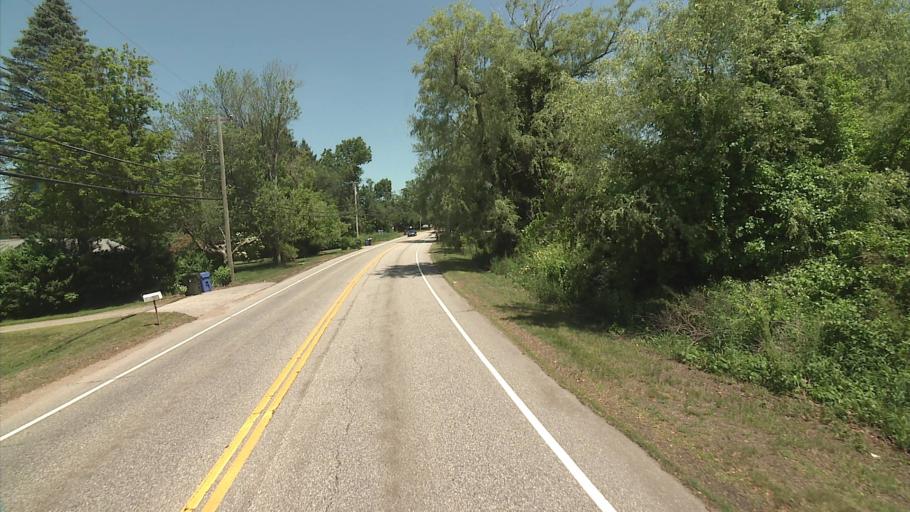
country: US
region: Connecticut
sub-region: Tolland County
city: Tolland
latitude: 41.8797
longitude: -72.4048
